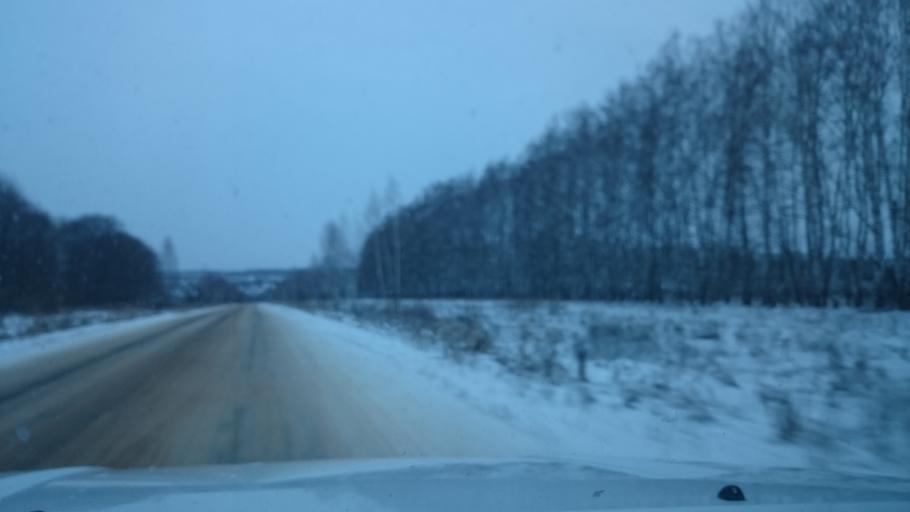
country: RU
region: Tula
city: Leninskiy
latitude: 54.2427
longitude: 37.2805
